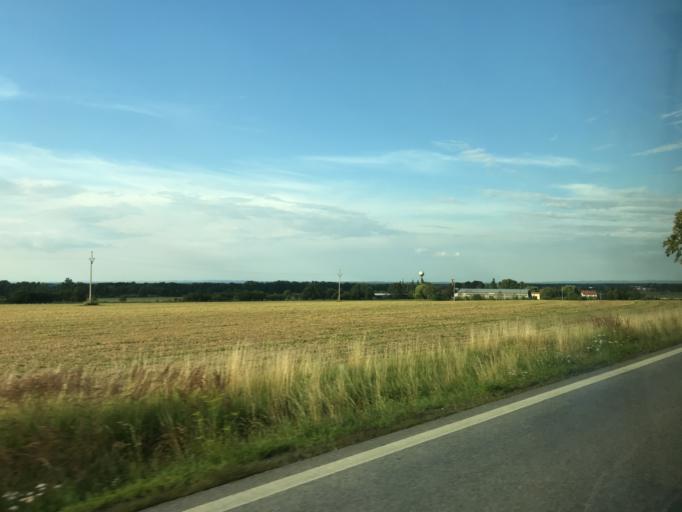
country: CZ
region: Jihocesky
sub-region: Okres Jindrichuv Hradec
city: Trebon
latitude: 48.9986
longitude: 14.7206
